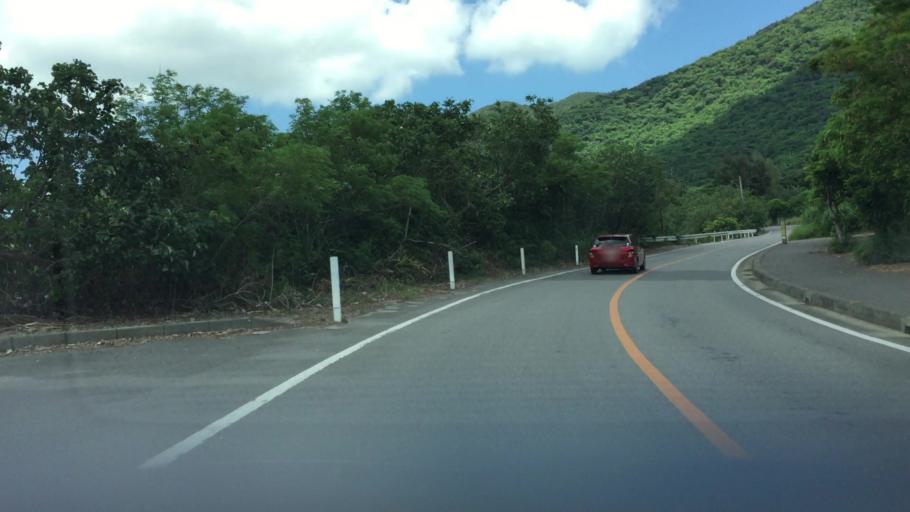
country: JP
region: Okinawa
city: Ishigaki
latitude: 24.4168
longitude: 124.1338
